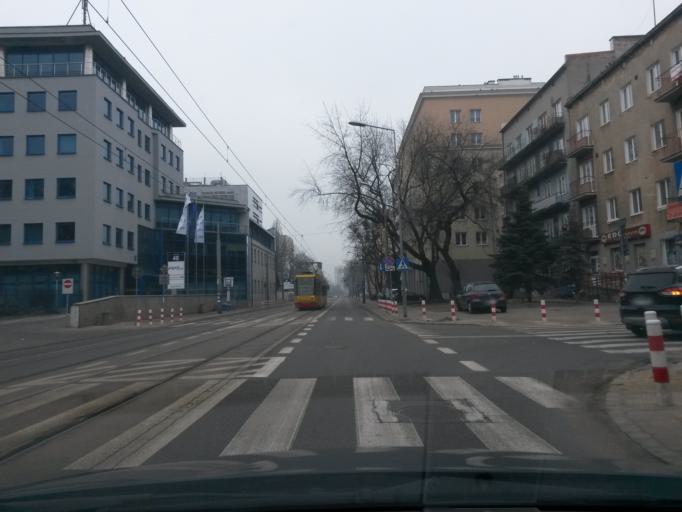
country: PL
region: Masovian Voivodeship
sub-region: Warszawa
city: Wola
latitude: 52.2409
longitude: 20.9705
